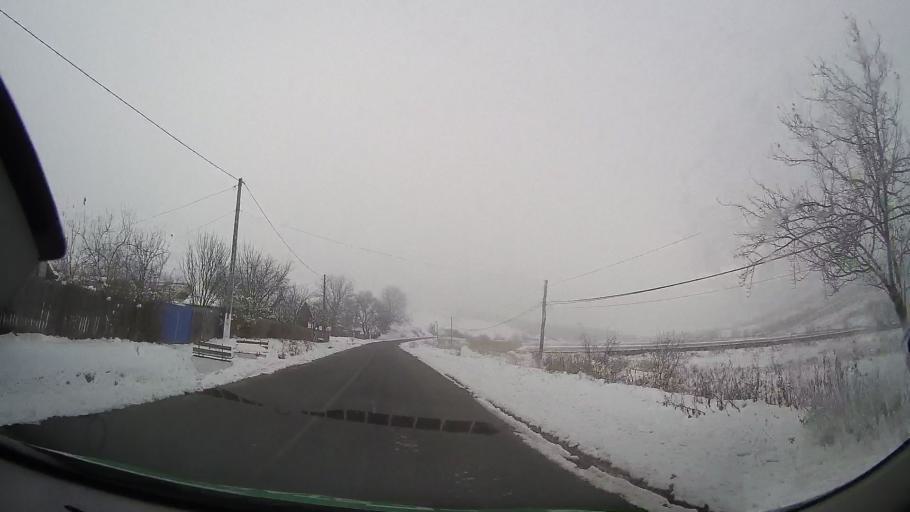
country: RO
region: Bacau
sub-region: Comuna Oncesti
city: Oncesti
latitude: 46.4839
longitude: 27.2560
